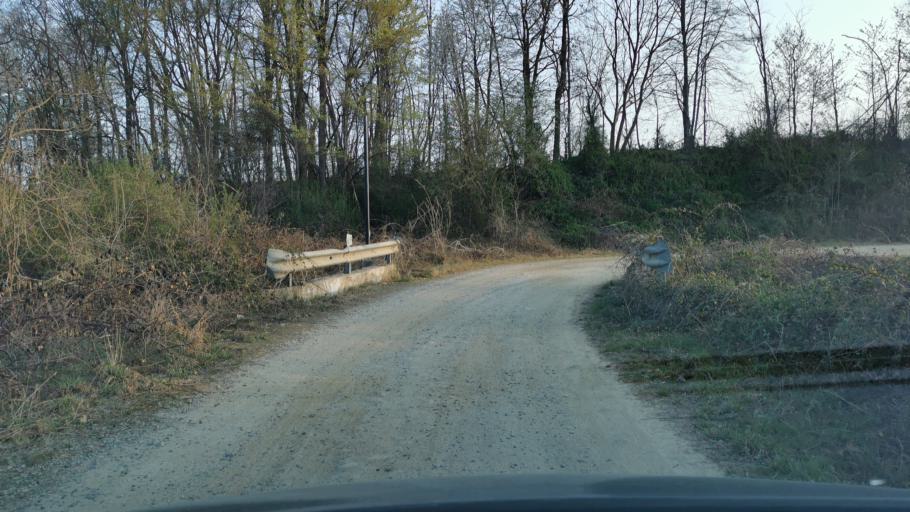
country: IT
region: Piedmont
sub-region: Provincia di Torino
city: Rivarossa
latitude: 45.2428
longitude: 7.6941
